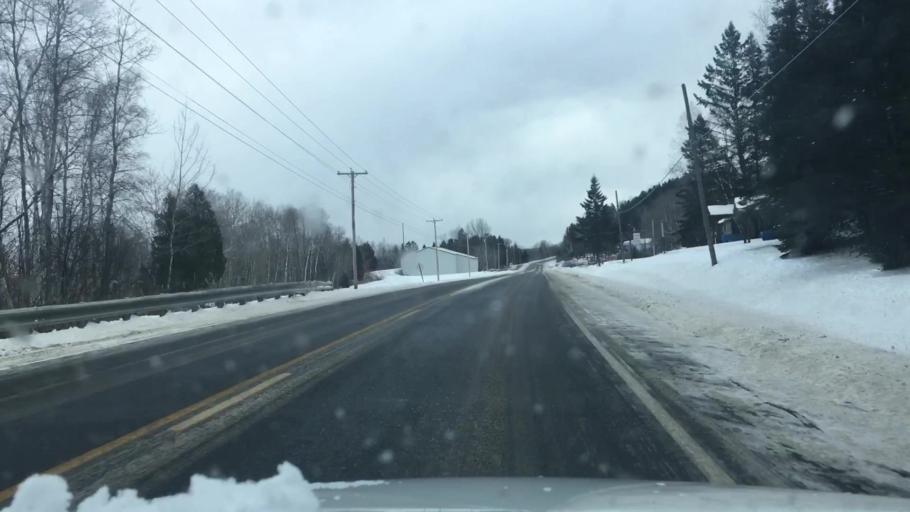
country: US
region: Maine
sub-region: Aroostook County
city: Madawaska
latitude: 47.3276
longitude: -68.1820
